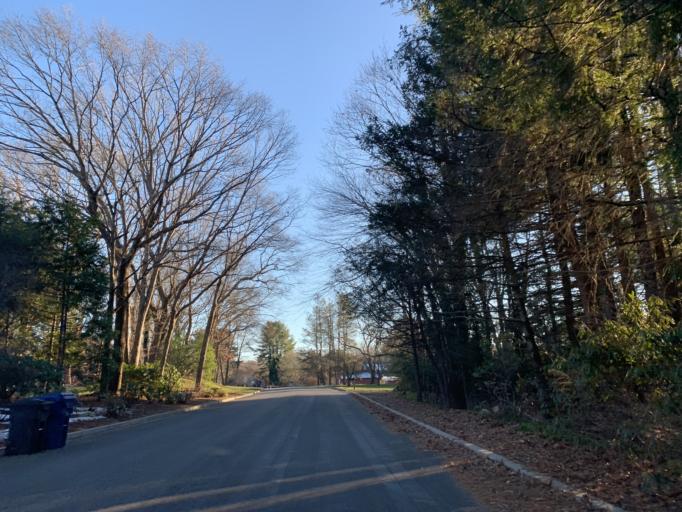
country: US
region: Rhode Island
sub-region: Washington County
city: Exeter
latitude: 41.6263
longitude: -71.5184
